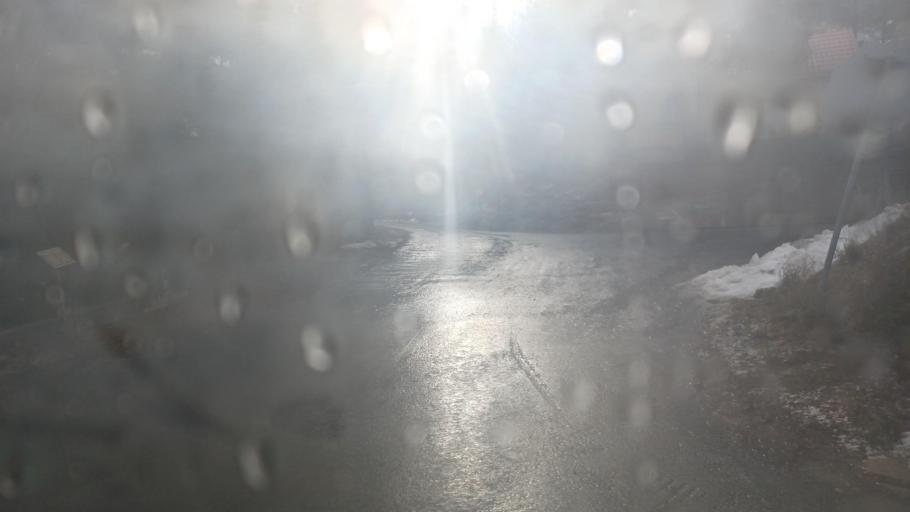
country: CY
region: Limassol
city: Kyperounta
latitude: 34.9432
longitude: 32.9601
